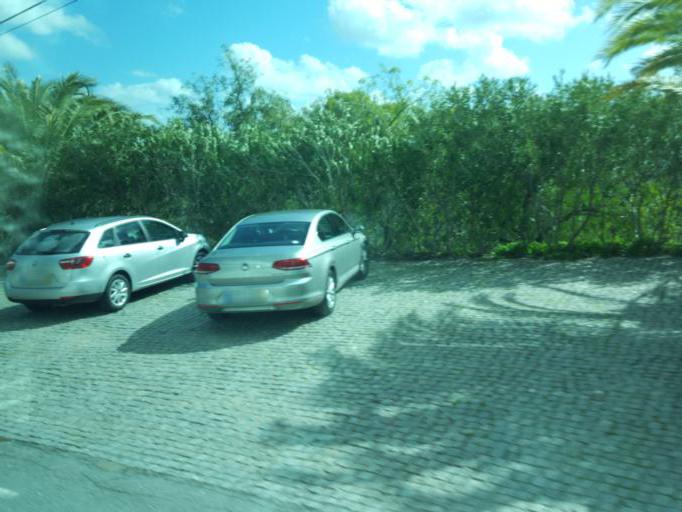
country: PT
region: Faro
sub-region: Monchique
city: Monchique
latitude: 37.2791
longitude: -8.5537
